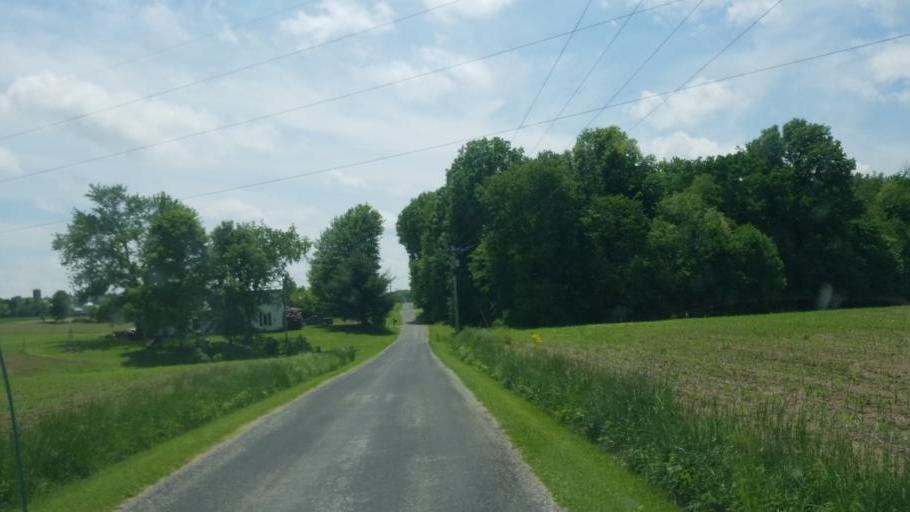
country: US
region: Ohio
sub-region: Ashland County
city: Ashland
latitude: 40.8376
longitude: -82.1938
